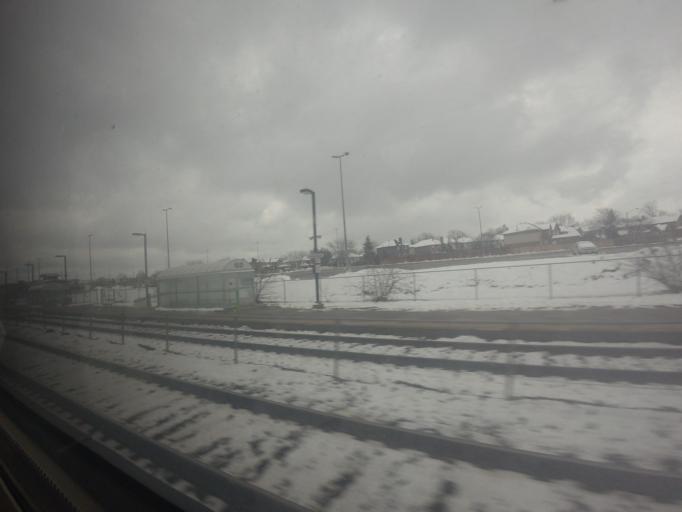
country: CA
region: Ontario
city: Scarborough
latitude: 43.7154
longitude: -79.2560
